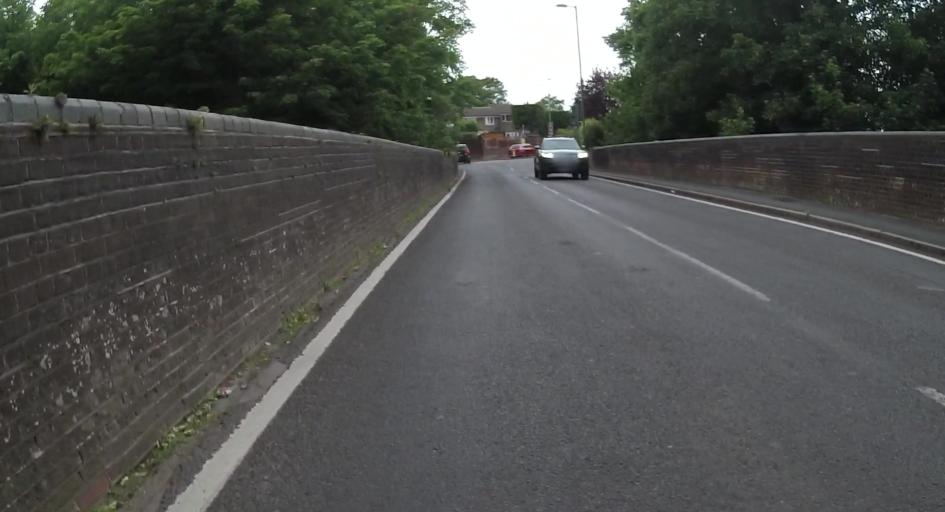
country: GB
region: England
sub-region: Hampshire
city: Aldershot
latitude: 51.2433
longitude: -0.7642
